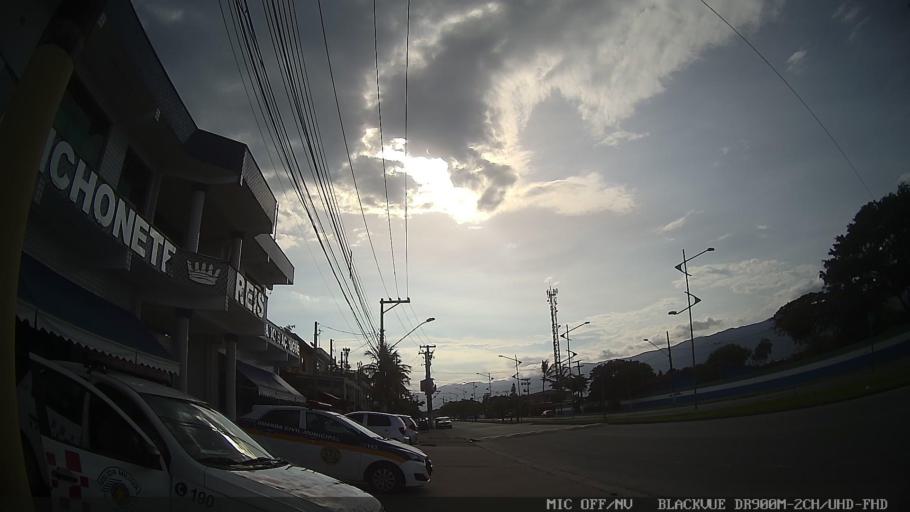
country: BR
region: Sao Paulo
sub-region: Bertioga
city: Bertioga
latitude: -23.8145
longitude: -46.0785
